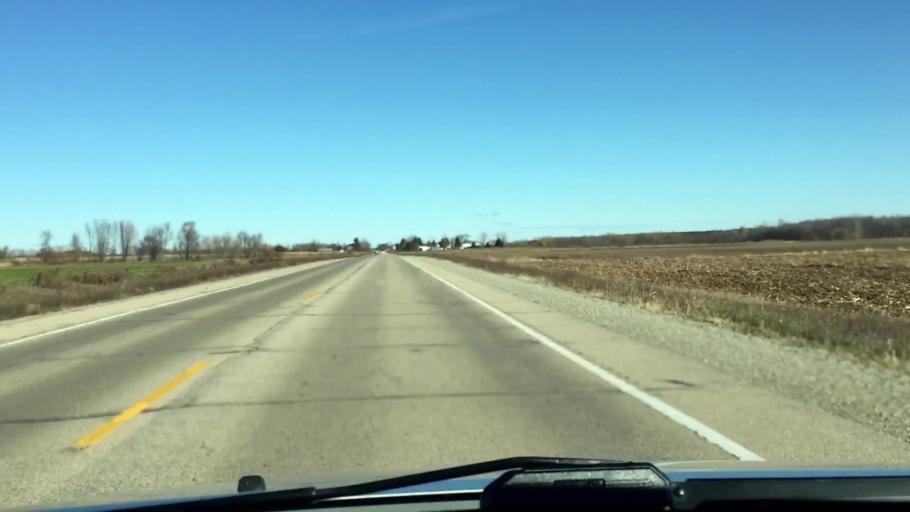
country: US
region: Wisconsin
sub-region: Brown County
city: Pulaski
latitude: 44.6312
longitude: -88.2202
